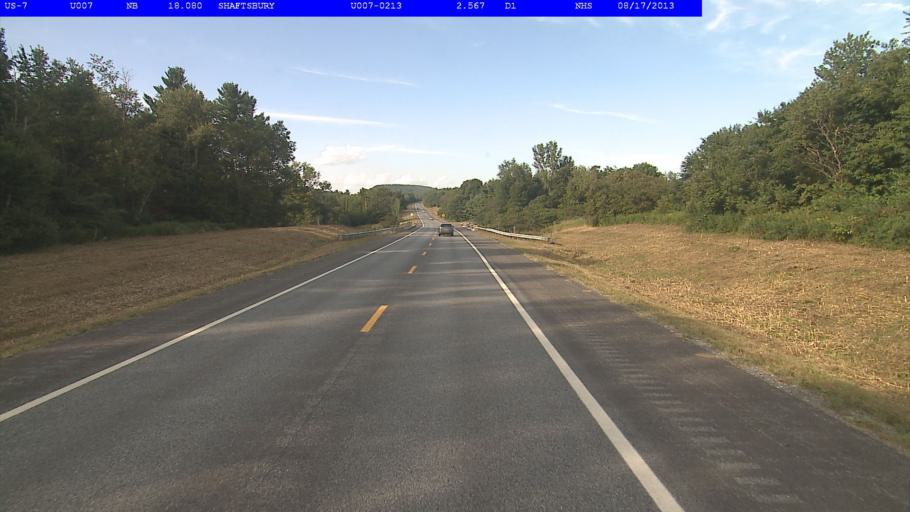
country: US
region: Vermont
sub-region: Bennington County
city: North Bennington
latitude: 42.9649
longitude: -73.1644
